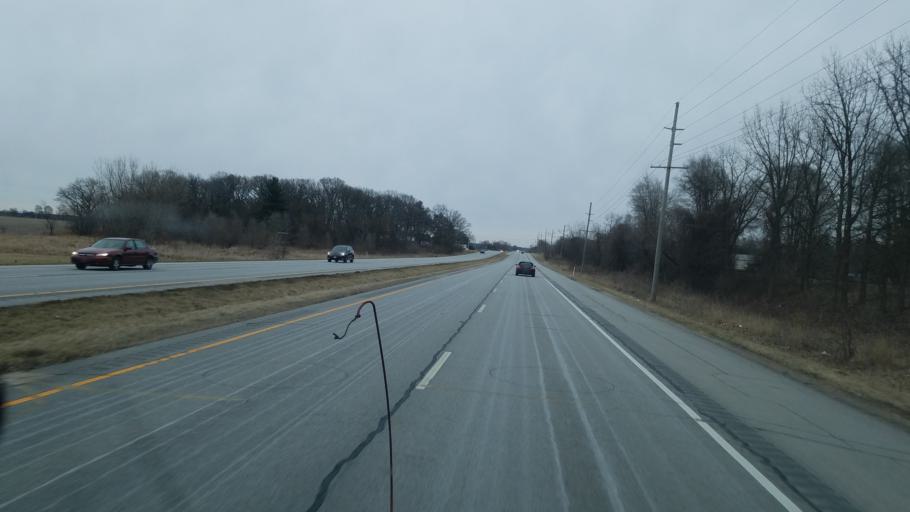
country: US
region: Indiana
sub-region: Porter County
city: Valparaiso
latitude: 41.4427
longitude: -86.9848
